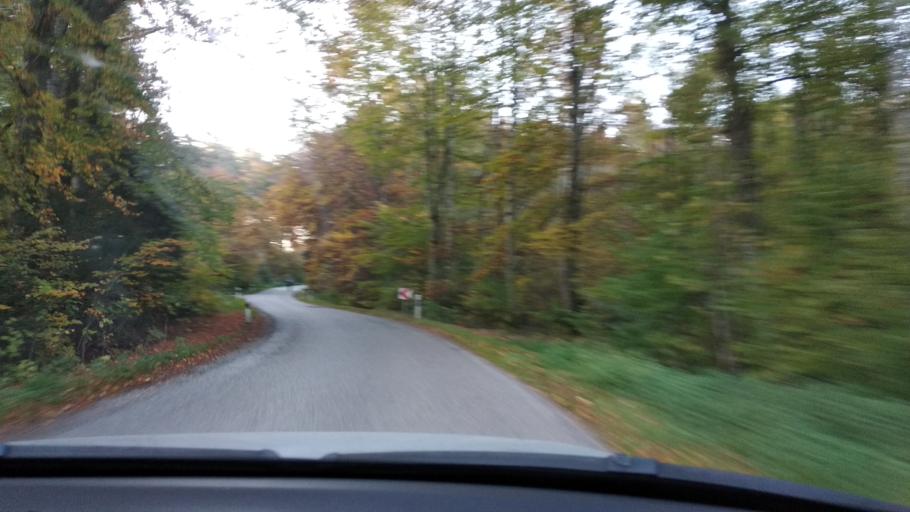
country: DE
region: Bavaria
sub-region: Upper Bavaria
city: Egmating
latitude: 47.9938
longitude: 11.8029
